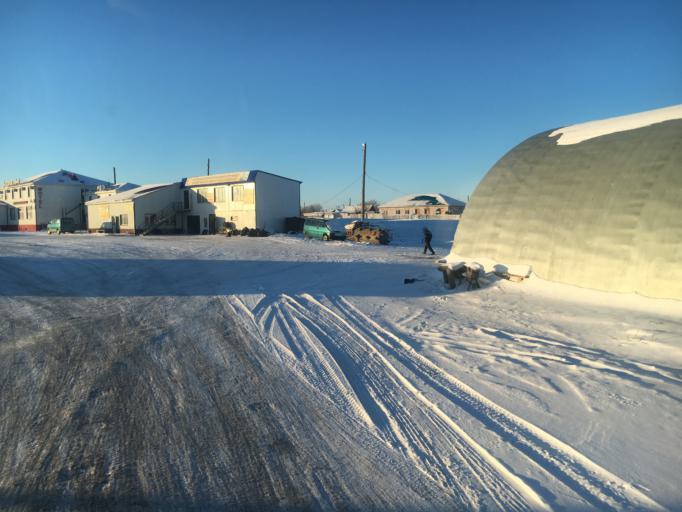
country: KZ
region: Aqtoebe
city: Khromtau
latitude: 50.2508
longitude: 58.4999
